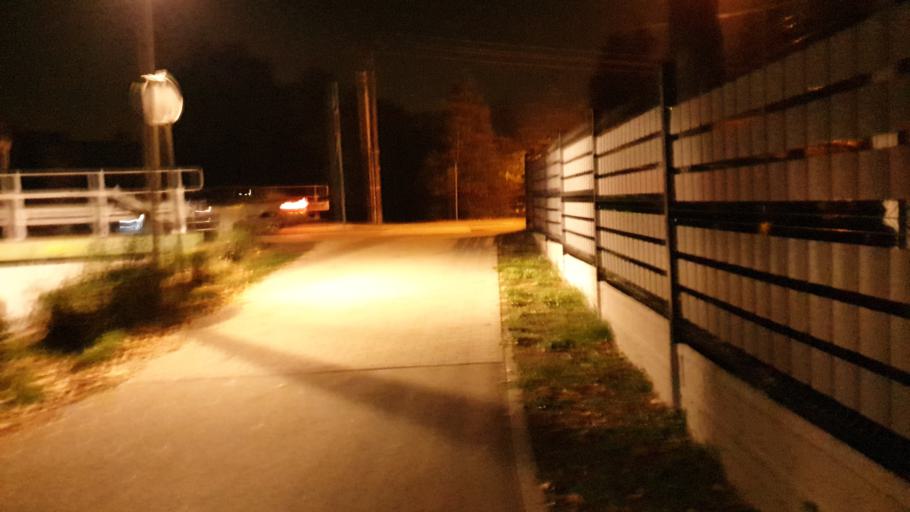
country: PL
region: Masovian Voivodeship
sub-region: Warszawa
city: Wesola
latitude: 52.2193
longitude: 21.2350
